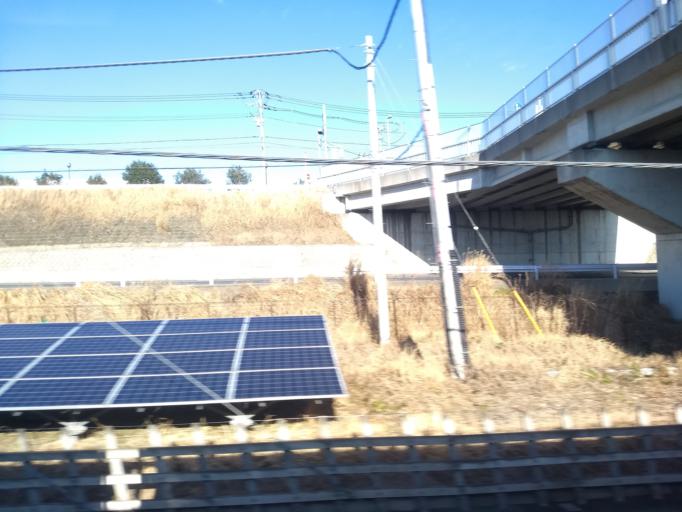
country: JP
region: Chiba
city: Sakura
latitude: 35.7954
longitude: 140.1839
